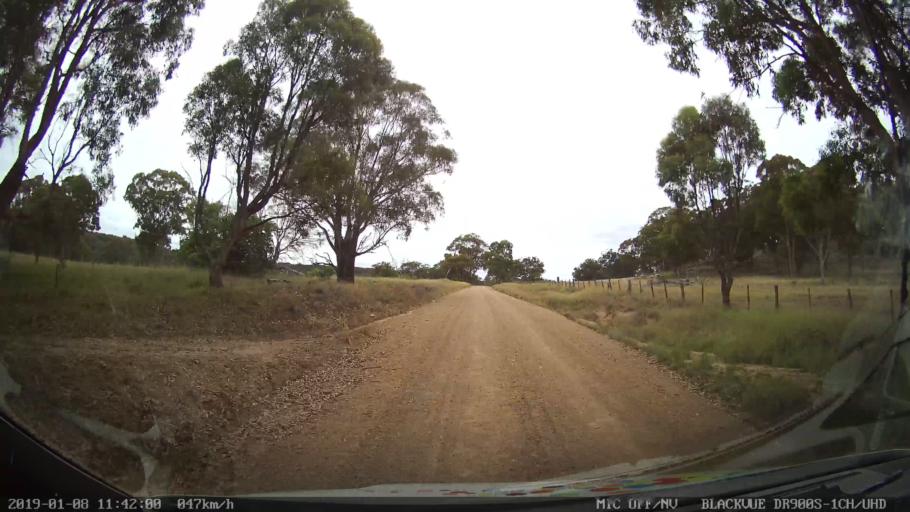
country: AU
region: New South Wales
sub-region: Armidale Dumaresq
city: Armidale
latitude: -30.3775
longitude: 151.5725
